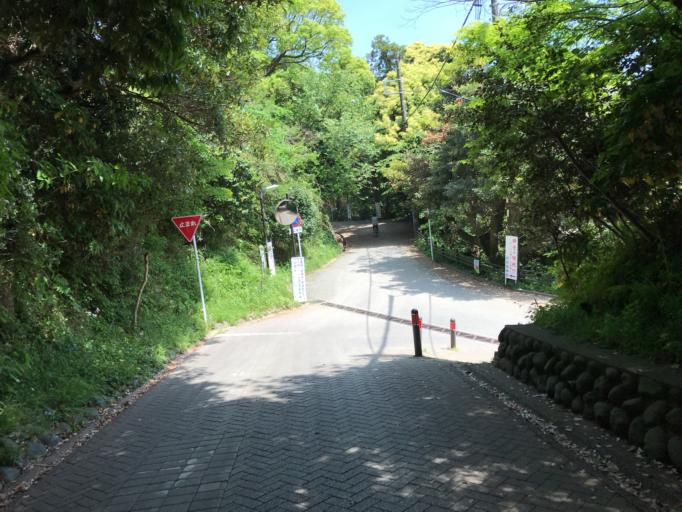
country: JP
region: Kanagawa
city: Kamakura
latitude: 35.3266
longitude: 139.5431
